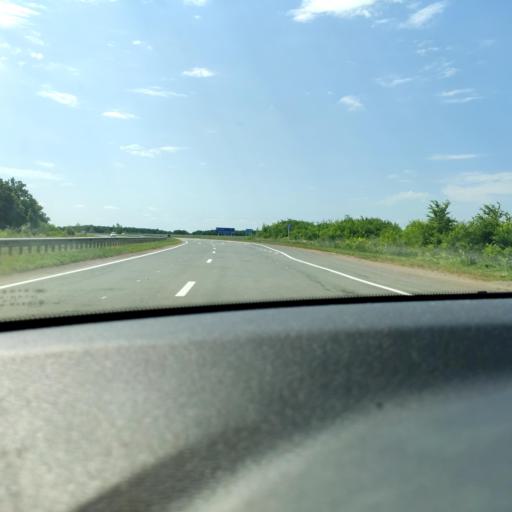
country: RU
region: Samara
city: Petra-Dubrava
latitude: 53.3394
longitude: 50.4370
